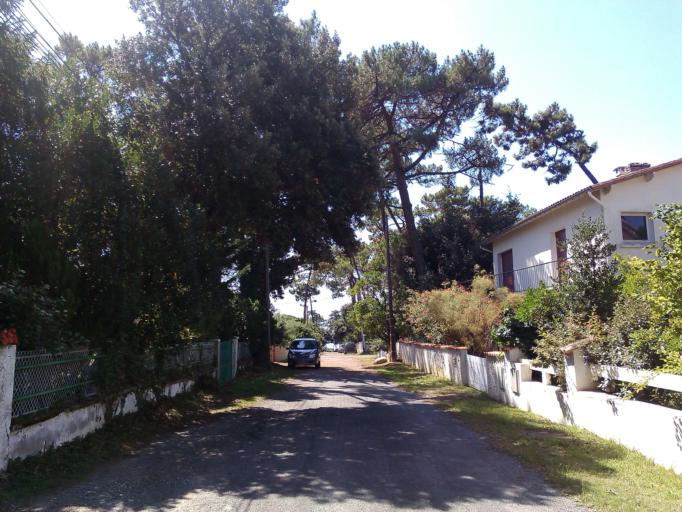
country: FR
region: Poitou-Charentes
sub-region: Departement de la Charente-Maritime
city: Vaux-sur-Mer
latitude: 45.6370
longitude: -1.0721
